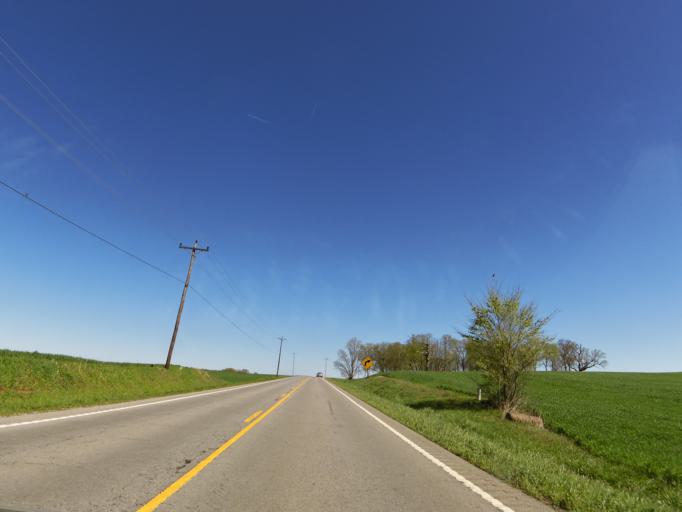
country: US
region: Tennessee
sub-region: Robertson County
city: Springfield
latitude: 36.5843
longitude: -86.8554
